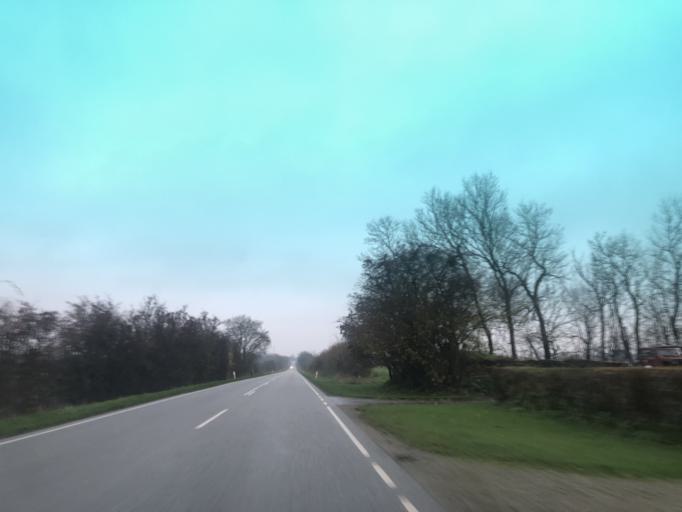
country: DK
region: South Denmark
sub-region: Kerteminde Kommune
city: Langeskov
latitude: 55.2265
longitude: 10.6269
